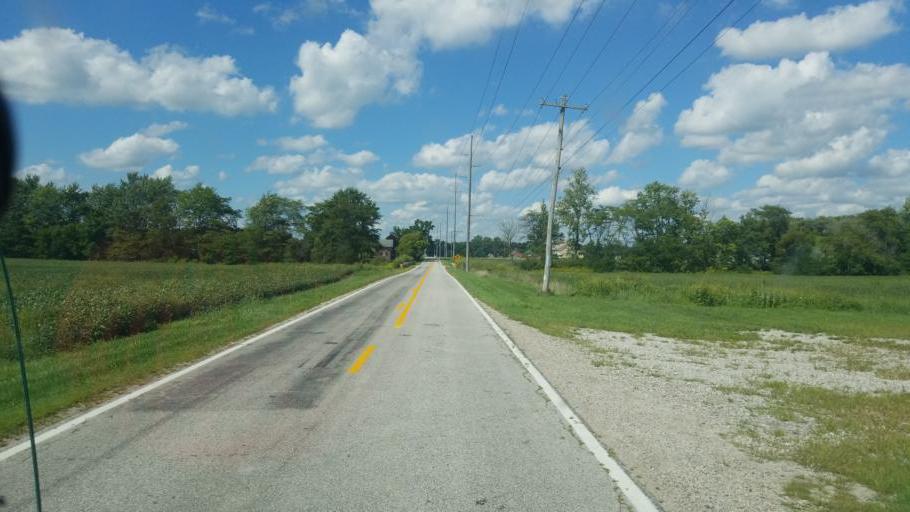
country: US
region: Ohio
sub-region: Delaware County
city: Delaware
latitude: 40.3130
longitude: -83.2000
